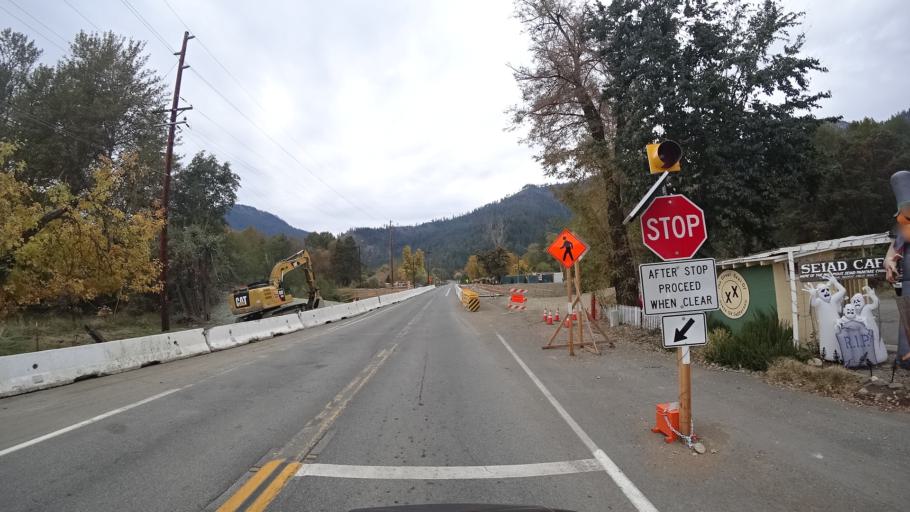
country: US
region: California
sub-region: Siskiyou County
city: Happy Camp
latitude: 41.8422
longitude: -123.1966
